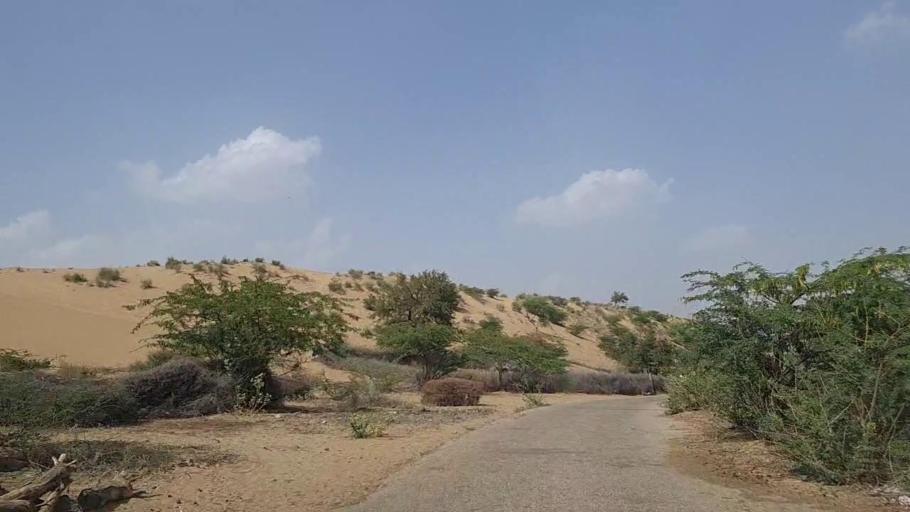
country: PK
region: Sindh
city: Islamkot
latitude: 24.7978
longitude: 70.1171
